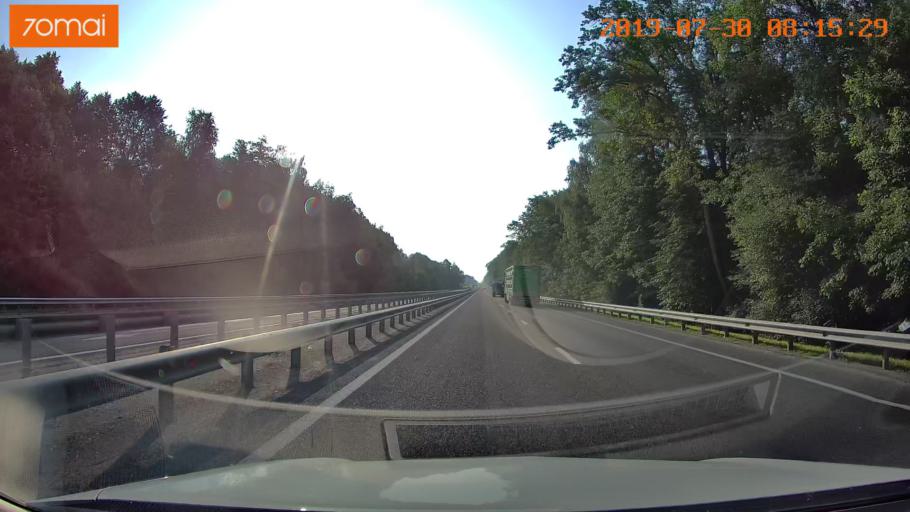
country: RU
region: Kaliningrad
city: Zheleznodorozhnyy
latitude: 54.6437
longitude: 21.3891
